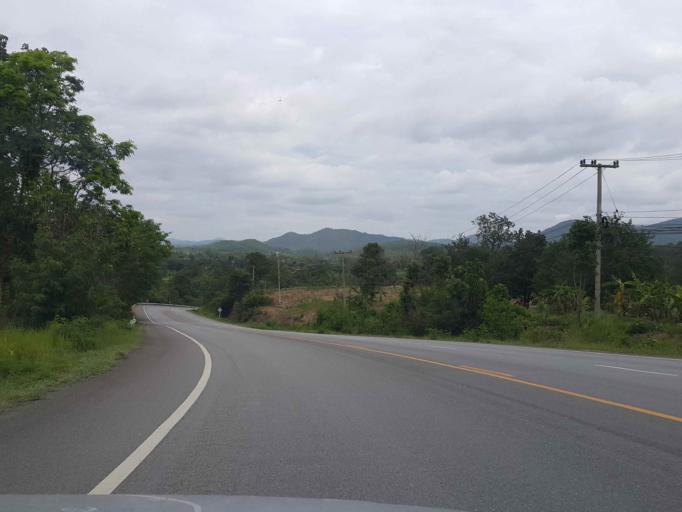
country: TH
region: Lamphun
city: Li
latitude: 17.7260
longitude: 99.0421
